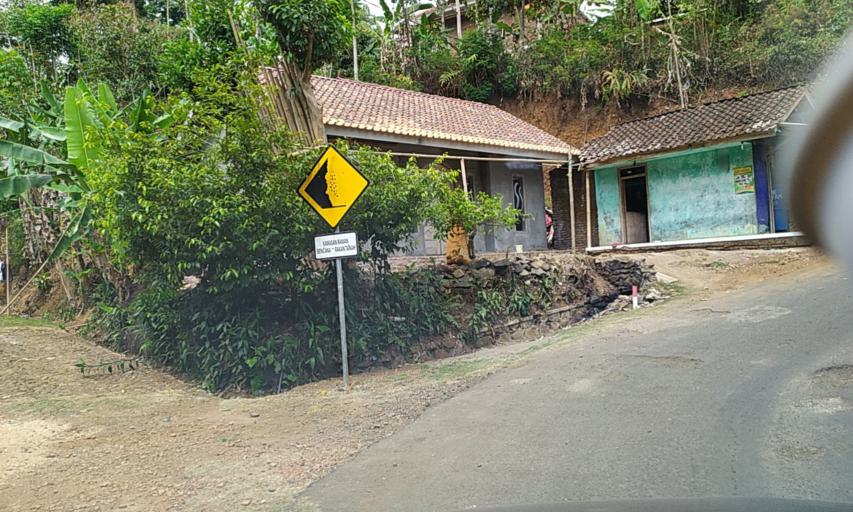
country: ID
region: Central Java
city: Kubang
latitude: -7.2707
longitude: 108.6459
